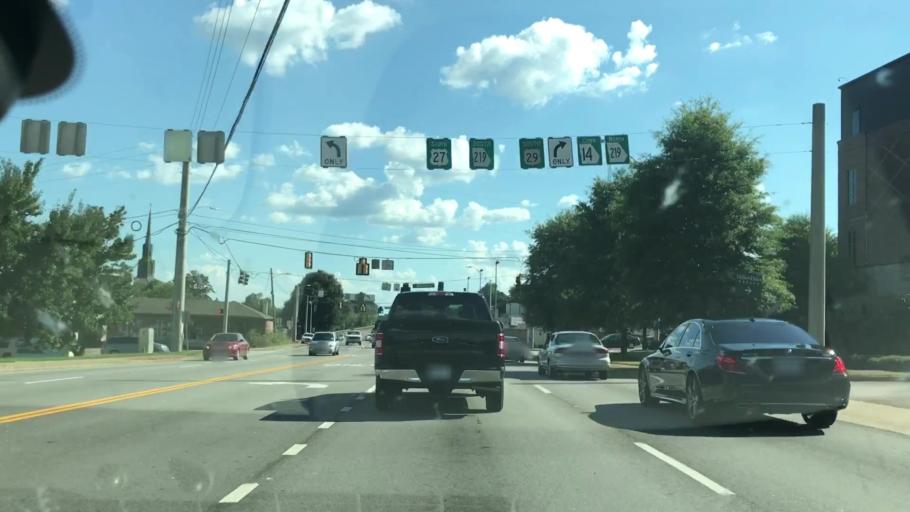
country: US
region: Georgia
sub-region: Troup County
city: La Grange
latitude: 33.0402
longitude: -85.0296
